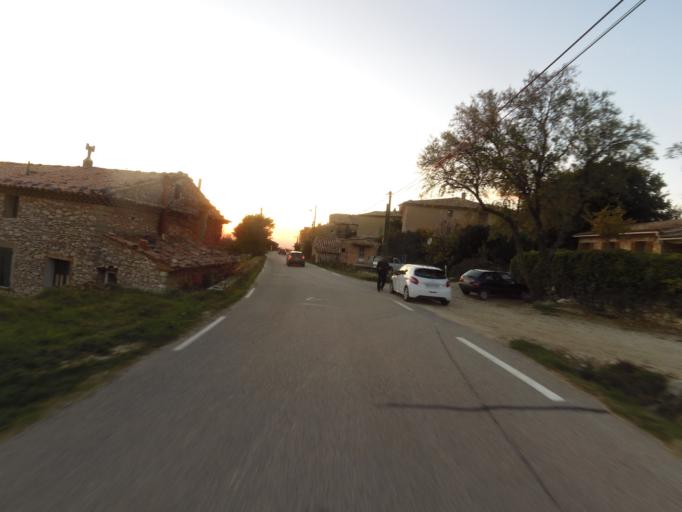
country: FR
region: Provence-Alpes-Cote d'Azur
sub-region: Departement du Vaucluse
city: Bedoin
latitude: 44.1170
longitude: 5.2366
